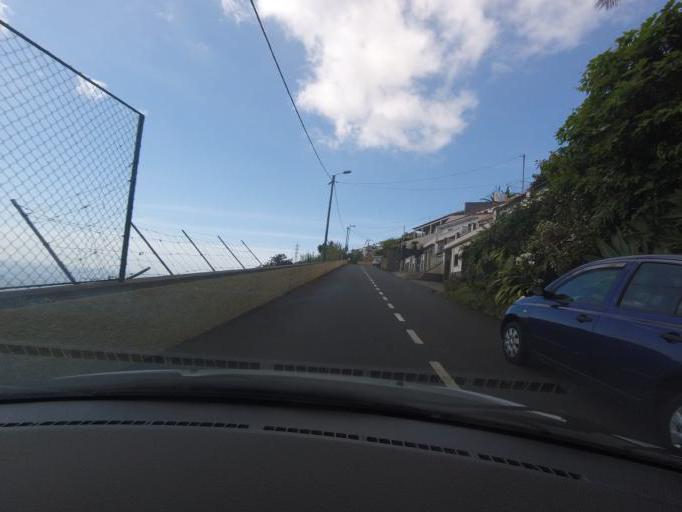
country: PT
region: Madeira
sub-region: Funchal
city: Nossa Senhora do Monte
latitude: 32.6724
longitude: -16.9411
